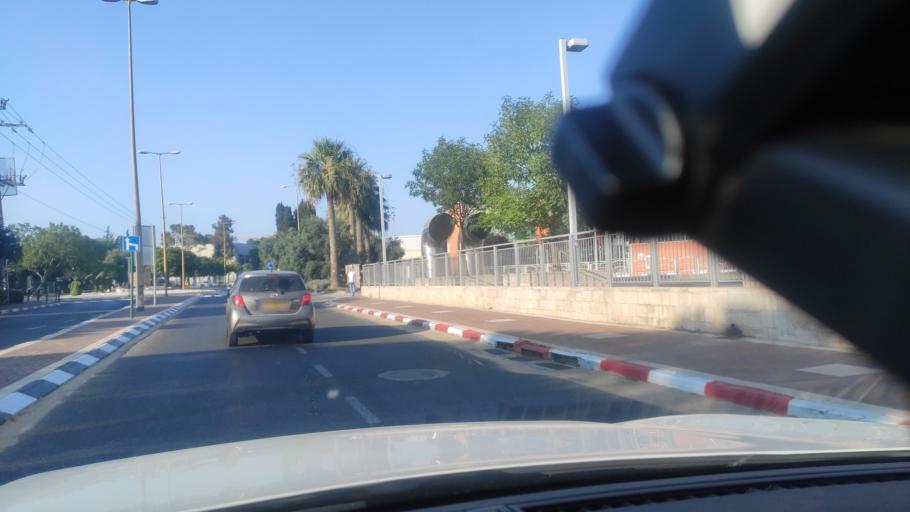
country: IL
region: Central District
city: Kfar Saba
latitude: 32.1770
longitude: 34.9352
